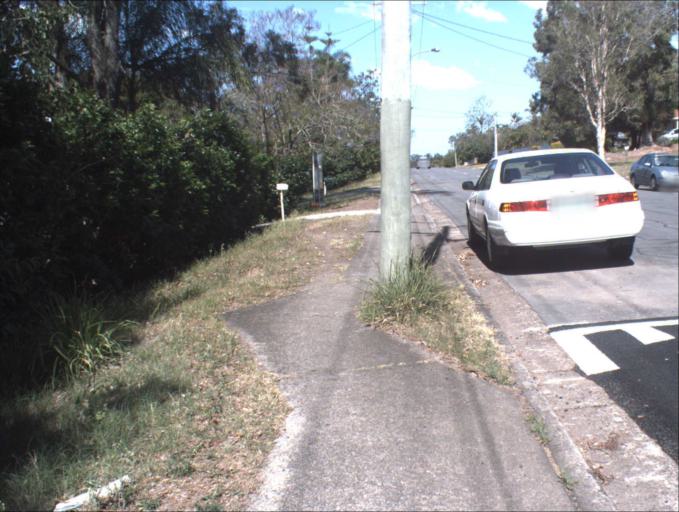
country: AU
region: Queensland
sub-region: Logan
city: Logan City
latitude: -27.6611
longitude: 153.1131
